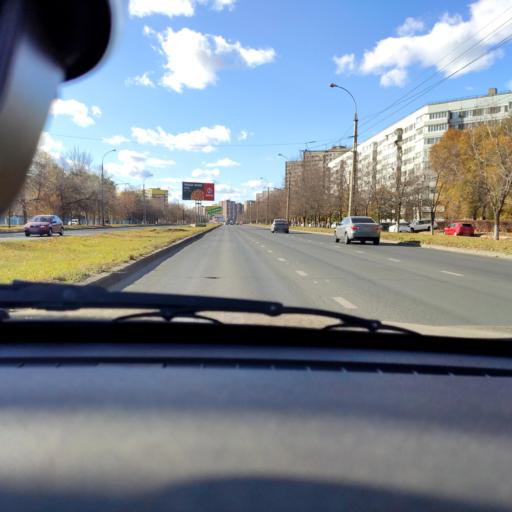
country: RU
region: Samara
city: Tol'yatti
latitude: 53.5230
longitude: 49.3226
